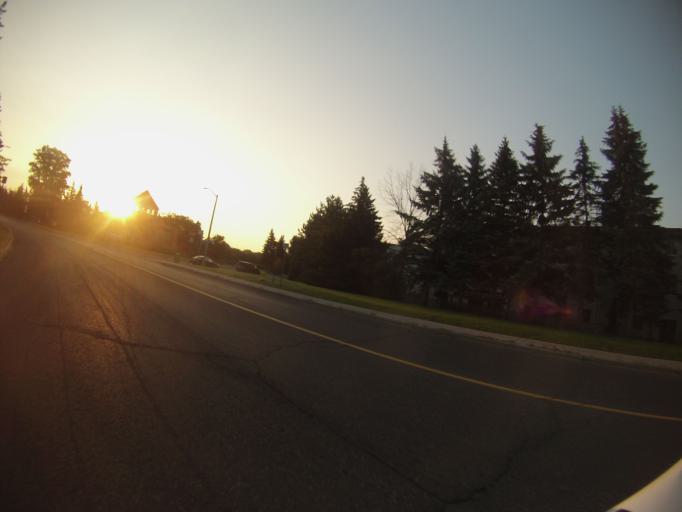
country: CA
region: Ontario
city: Ottawa
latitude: 45.3652
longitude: -75.6284
